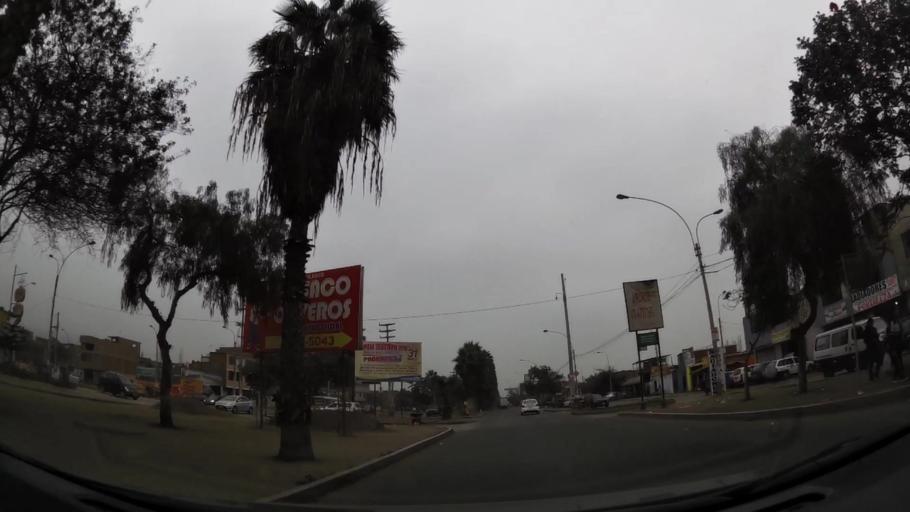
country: PE
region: Lima
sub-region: Lima
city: Urb. Santo Domingo
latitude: -11.9060
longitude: -77.0429
